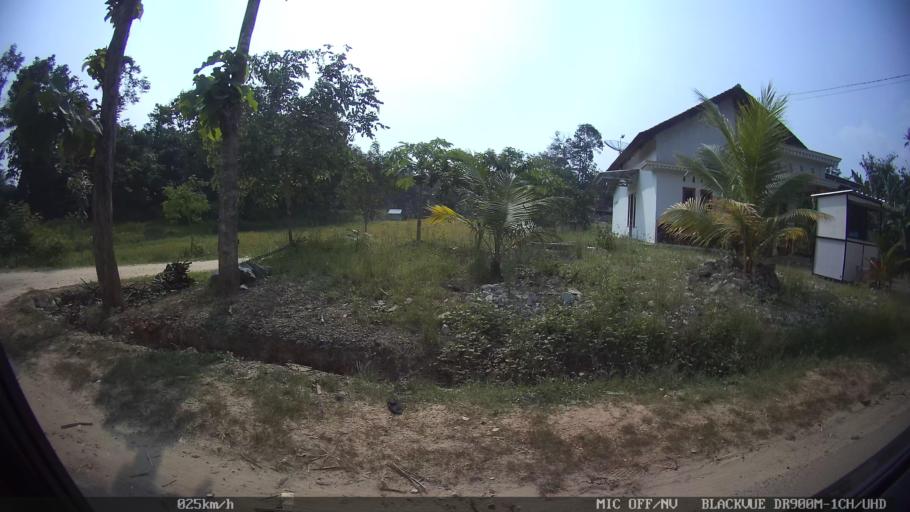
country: ID
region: Lampung
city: Pringsewu
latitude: -5.4052
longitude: 104.9922
